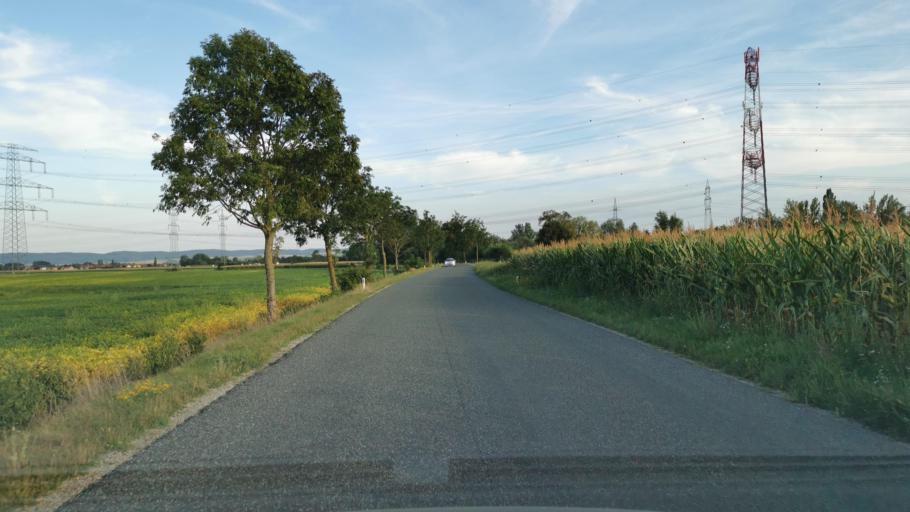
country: AT
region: Lower Austria
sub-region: Politischer Bezirk Tulln
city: Langenrohr
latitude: 48.3269
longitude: 15.9855
